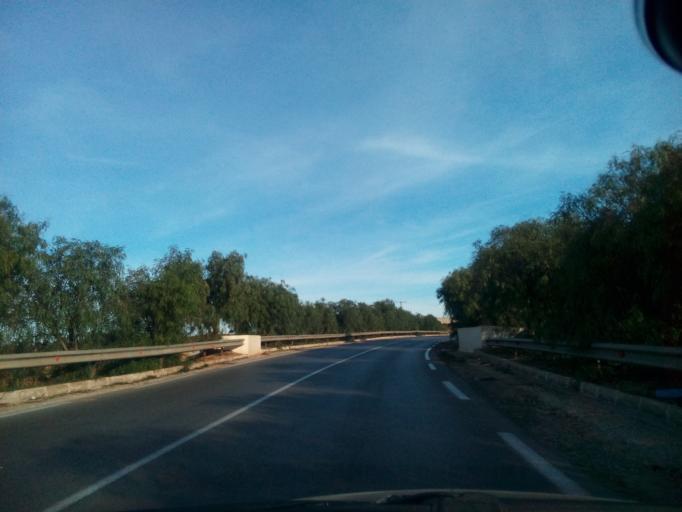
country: DZ
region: Mostaganem
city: Mostaganem
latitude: 35.8513
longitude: 0.1648
